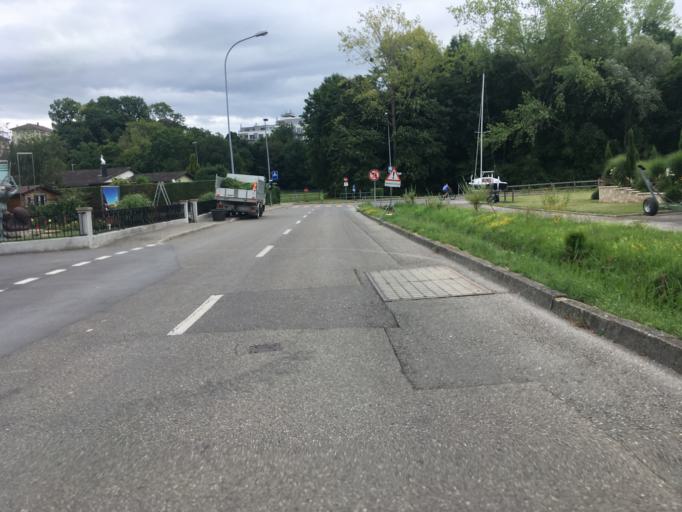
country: CH
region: Fribourg
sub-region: Broye District
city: Estavayer-le-Lac
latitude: 46.8470
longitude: 6.8382
